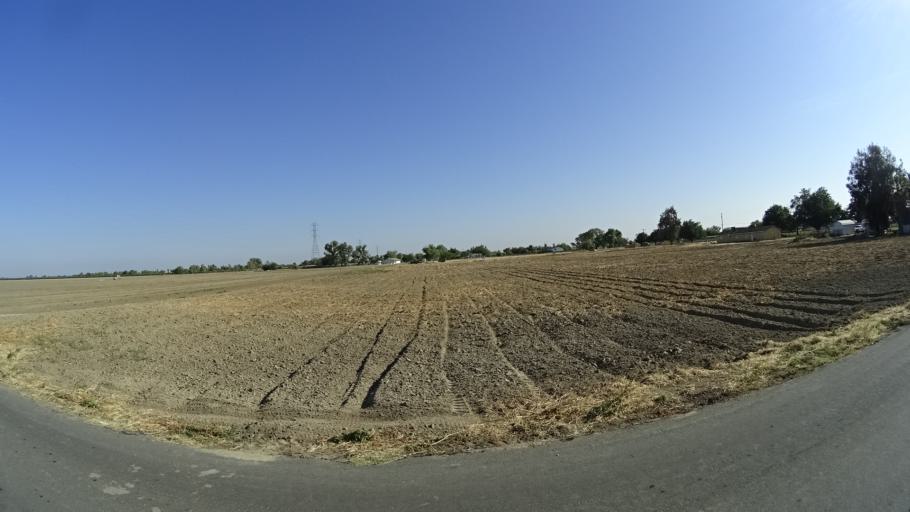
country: US
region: California
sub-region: Fresno County
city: Riverdale
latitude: 36.3766
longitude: -119.8887
